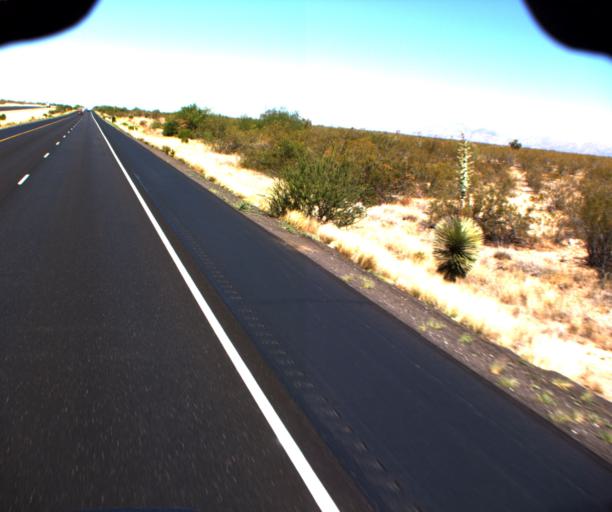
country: US
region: Arizona
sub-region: Yavapai County
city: Congress
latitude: 34.0596
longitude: -112.8588
